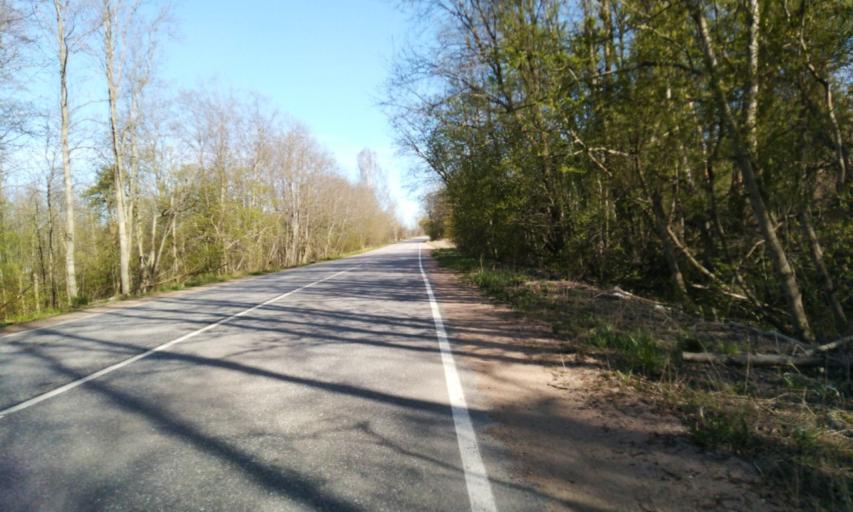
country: RU
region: Leningrad
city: Leskolovo
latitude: 60.3263
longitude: 30.4263
